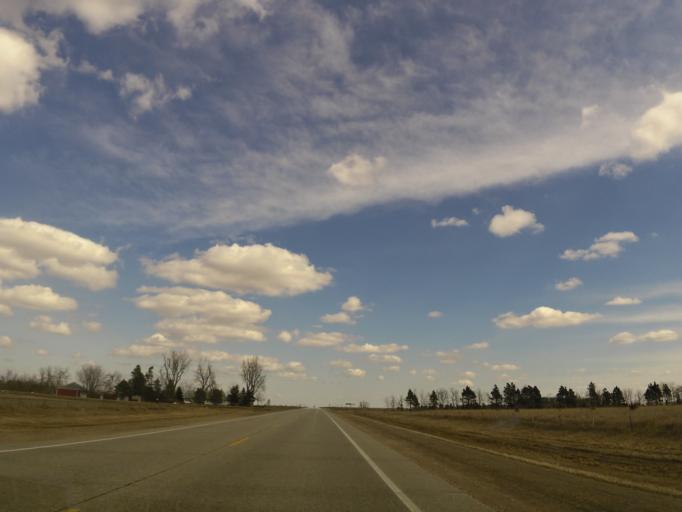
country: US
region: South Dakota
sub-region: Deuel County
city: Clear Lake
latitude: 44.8899
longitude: -96.8543
